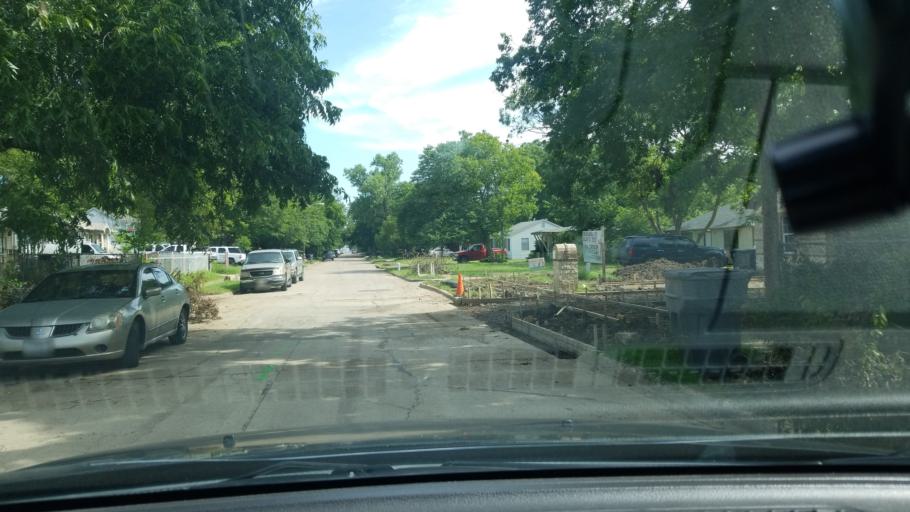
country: US
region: Texas
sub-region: Dallas County
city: Balch Springs
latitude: 32.7643
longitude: -96.6760
